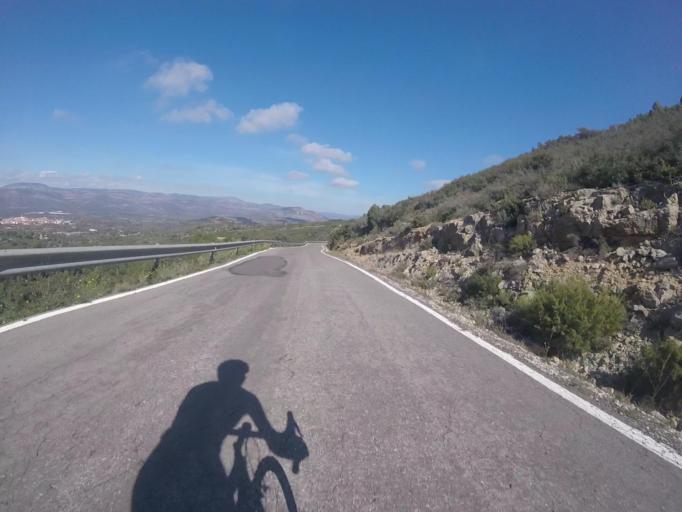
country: ES
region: Valencia
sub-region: Provincia de Castello
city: Albocasser
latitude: 40.3481
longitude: 0.0495
